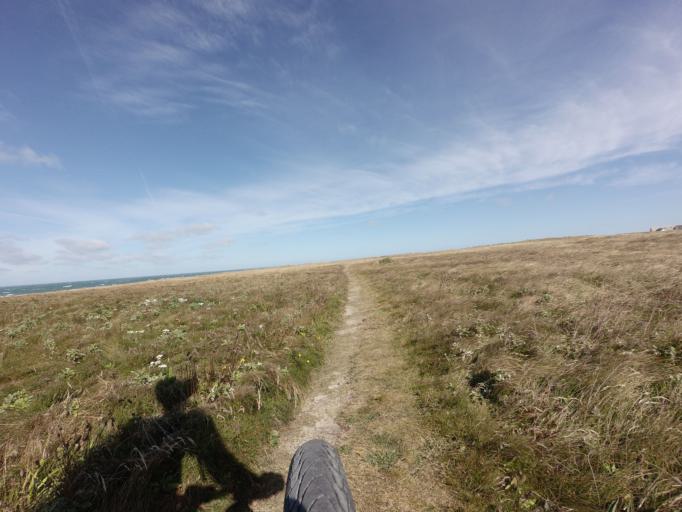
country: DK
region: North Denmark
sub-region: Jammerbugt Kommune
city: Pandrup
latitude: 57.3905
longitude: 9.7284
